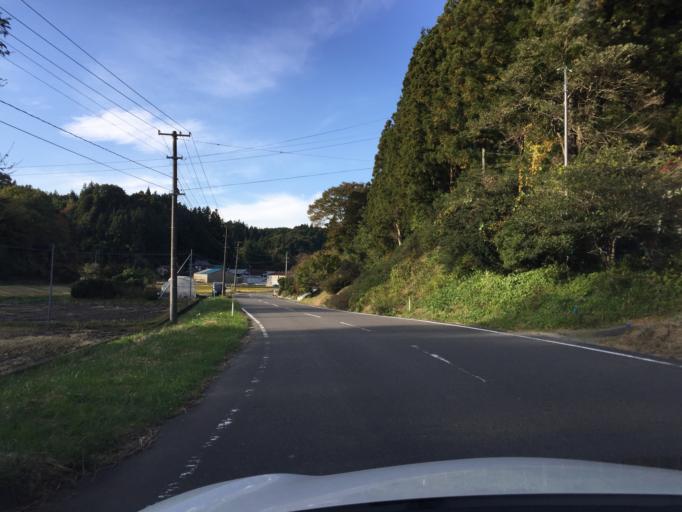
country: JP
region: Fukushima
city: Ishikawa
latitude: 37.2074
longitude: 140.5834
